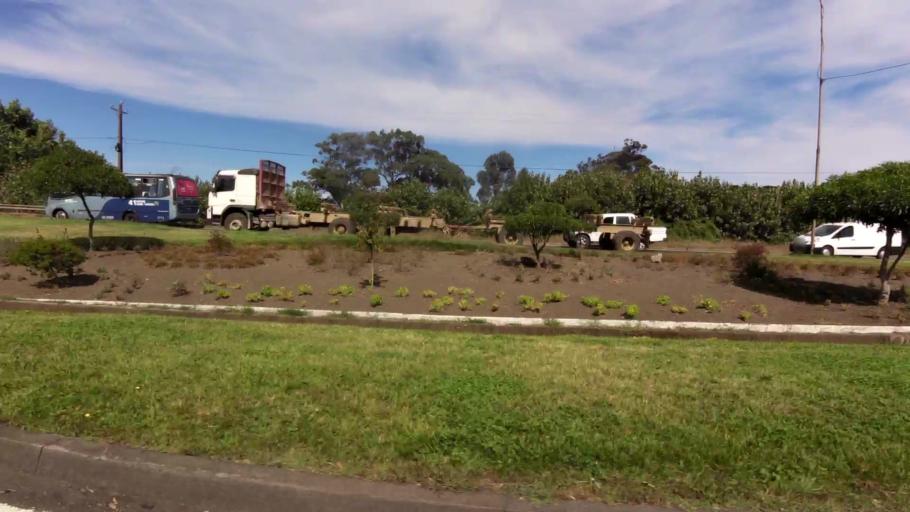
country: CL
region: Biobio
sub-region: Provincia de Concepcion
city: Talcahuano
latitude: -36.7712
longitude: -73.1145
